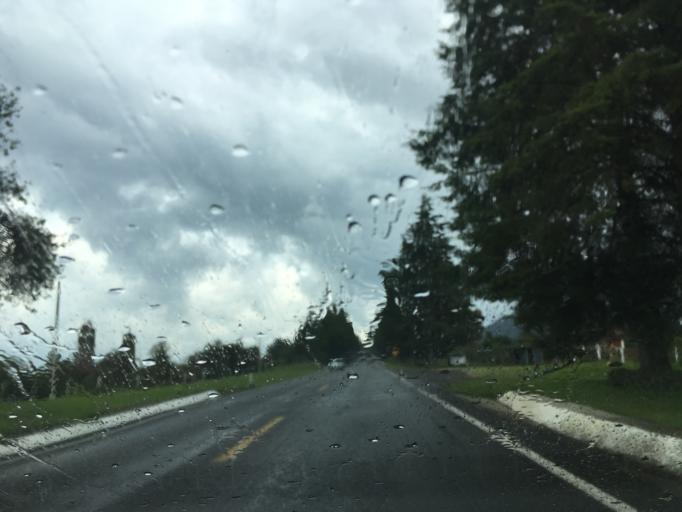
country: MX
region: Michoacan
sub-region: Patzcuaro
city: Santa Ana Chapitiro
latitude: 19.5125
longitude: -101.6719
